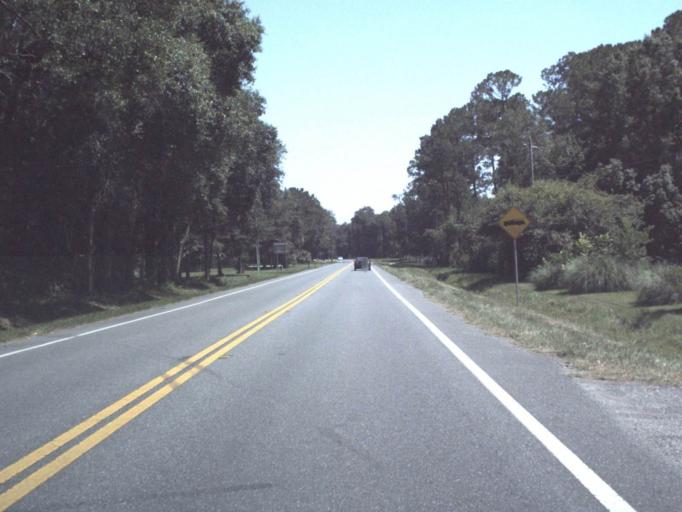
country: US
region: Florida
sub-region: Baker County
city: Macclenny
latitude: 30.3365
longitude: -82.1251
